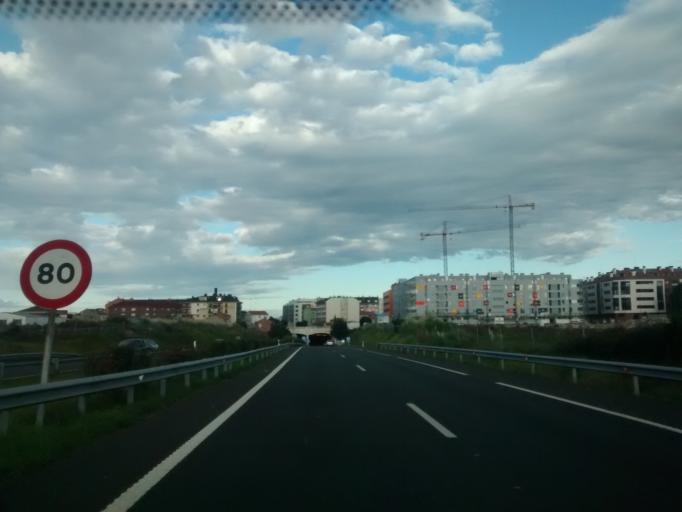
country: ES
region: Cantabria
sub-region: Provincia de Cantabria
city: Santander
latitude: 43.4638
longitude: -3.8464
